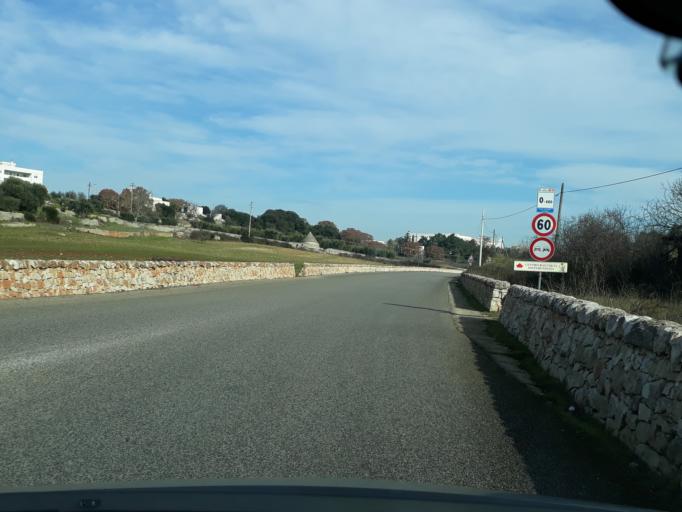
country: IT
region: Apulia
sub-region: Provincia di Bari
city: Locorotondo
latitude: 40.7495
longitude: 17.3351
